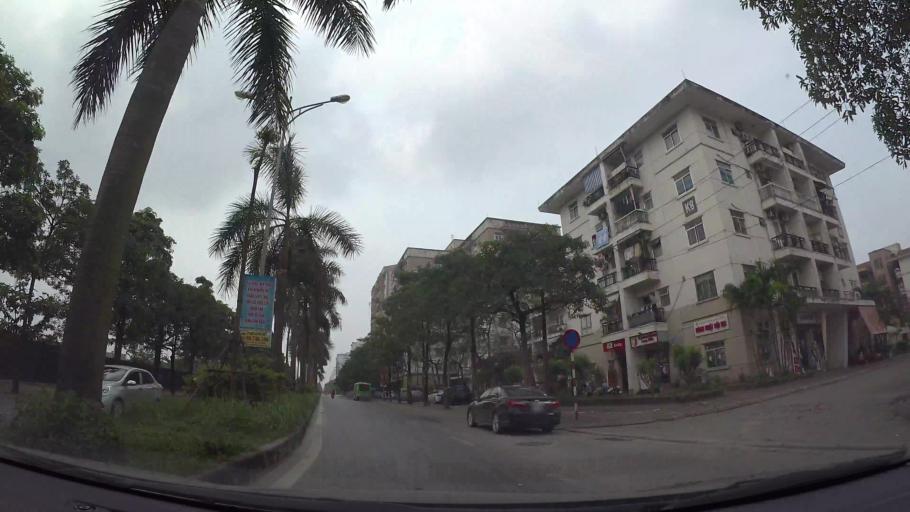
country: VN
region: Ha Noi
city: Trau Quy
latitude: 21.0652
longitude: 105.9077
